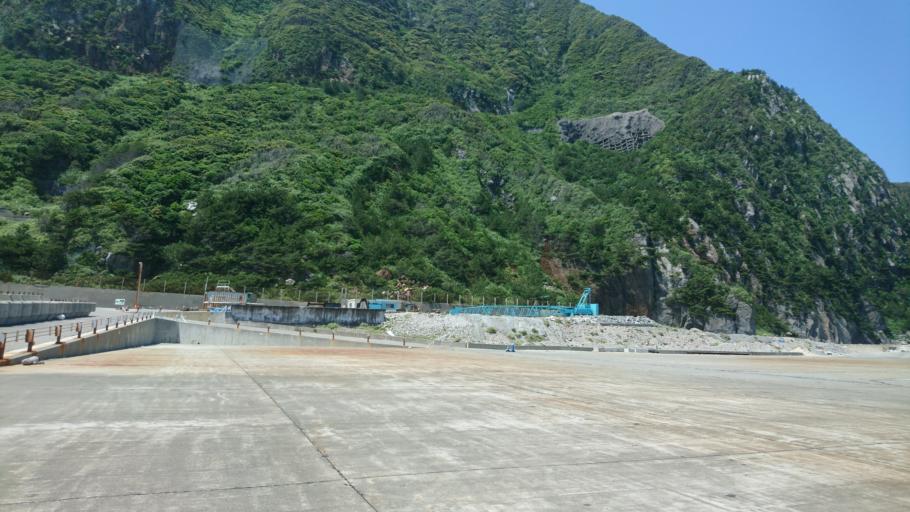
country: JP
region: Shizuoka
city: Shimoda
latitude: 34.3957
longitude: 139.2828
